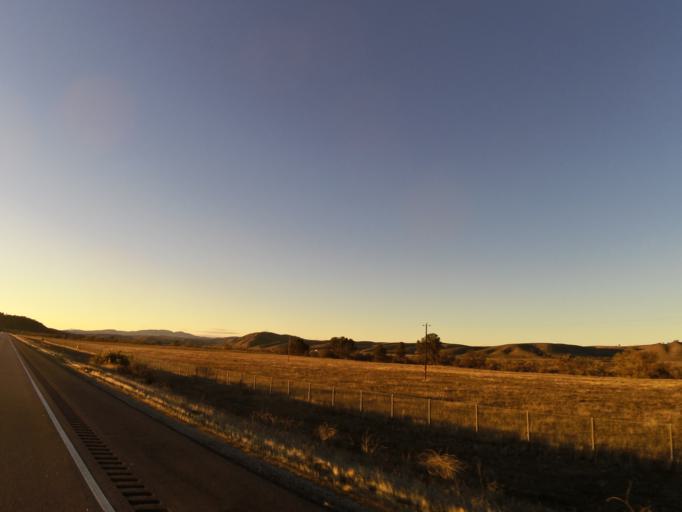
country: US
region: California
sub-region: San Luis Obispo County
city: San Miguel
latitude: 35.8530
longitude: -120.7780
